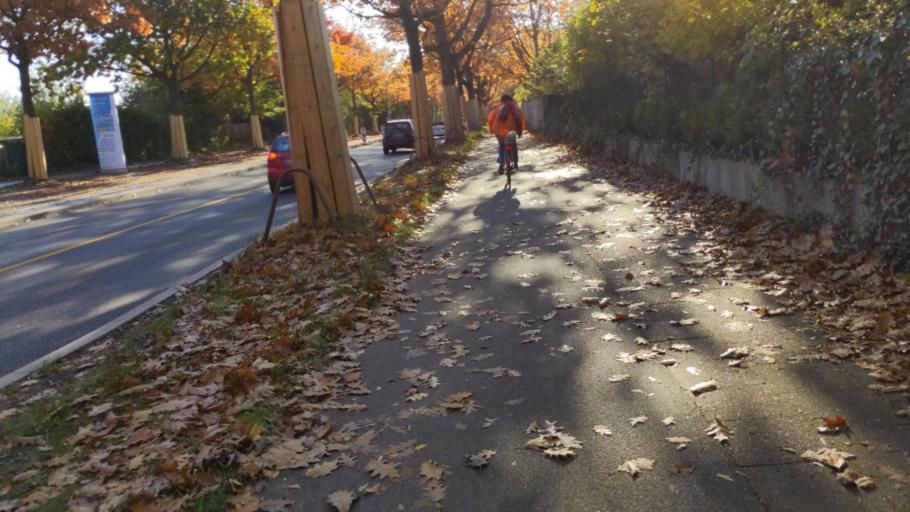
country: DE
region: Schleswig-Holstein
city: Luebeck
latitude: 53.8587
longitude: 10.7093
